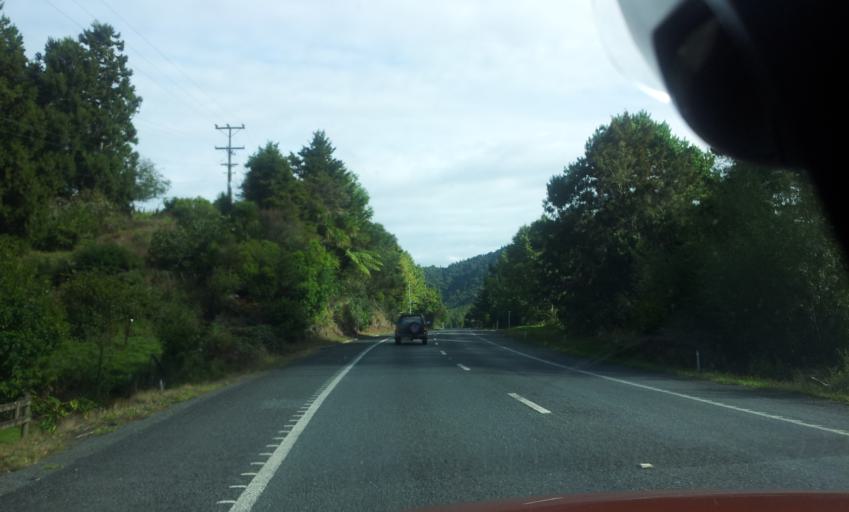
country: NZ
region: Auckland
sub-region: Auckland
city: Warkworth
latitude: -36.3779
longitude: 174.6336
